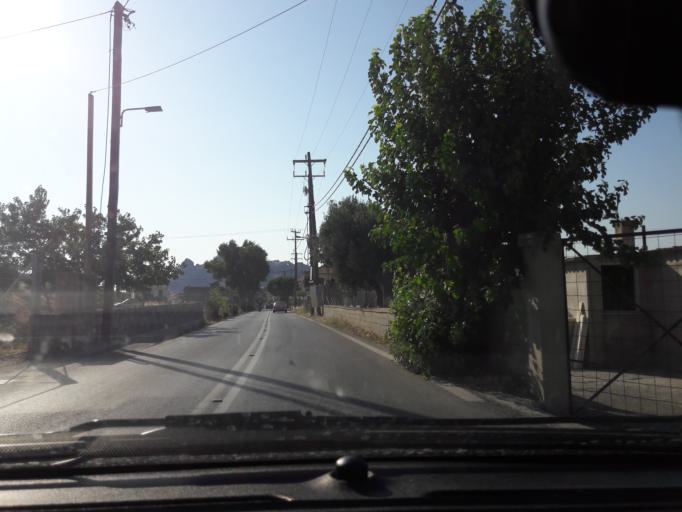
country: GR
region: North Aegean
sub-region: Nomos Lesvou
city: Myrina
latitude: 39.8712
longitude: 25.0683
